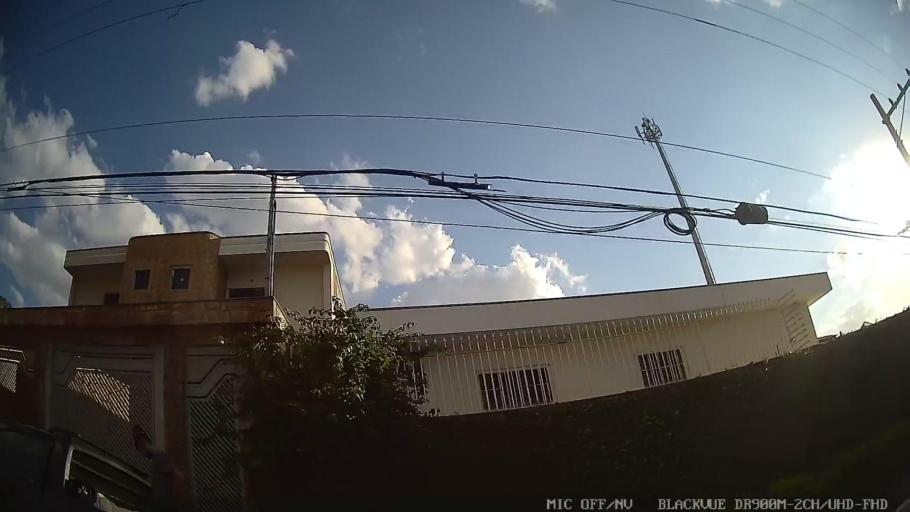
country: BR
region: Sao Paulo
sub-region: Sao Caetano Do Sul
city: Sao Caetano do Sul
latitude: -23.5597
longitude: -46.5443
